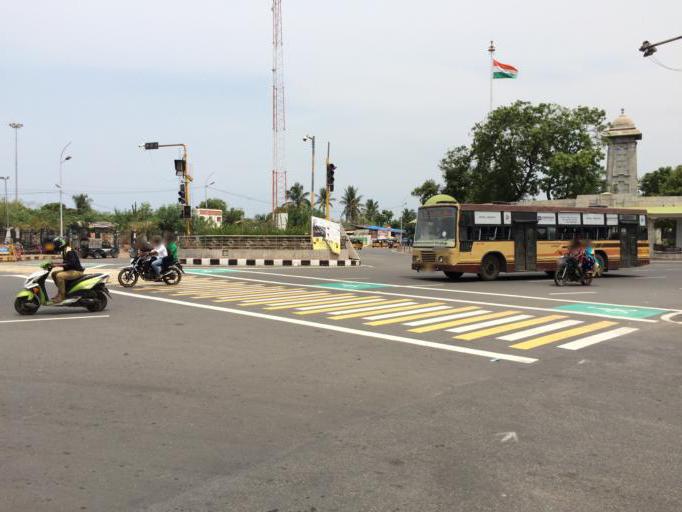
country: IN
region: Tamil Nadu
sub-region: Chennai
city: Chennai
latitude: 13.0744
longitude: 80.2857
